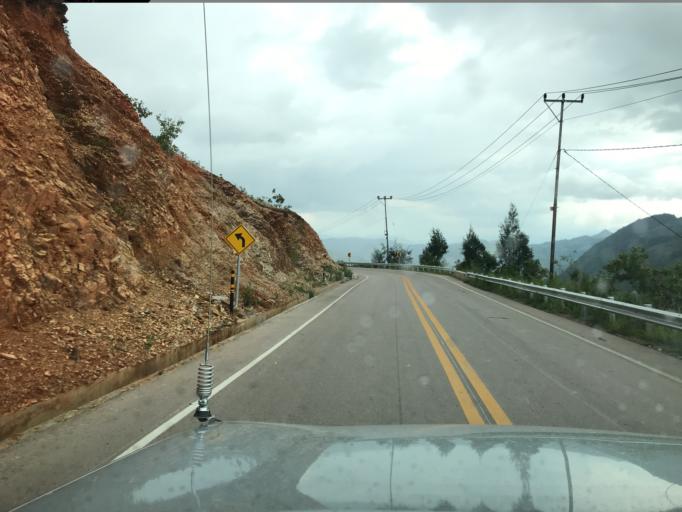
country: TL
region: Aileu
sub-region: Aileu Villa
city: Aileu
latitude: -8.8093
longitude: 125.5974
